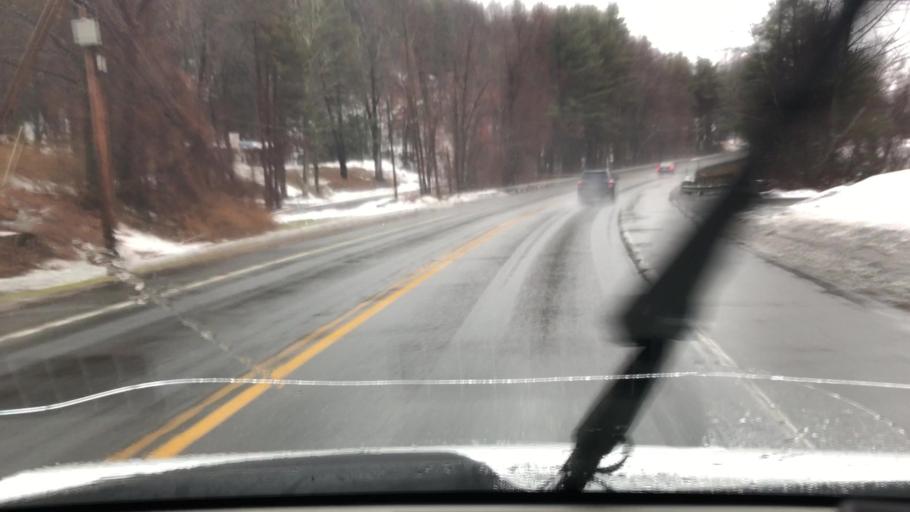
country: US
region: Massachusetts
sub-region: Franklin County
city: Shelburne Falls
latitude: 42.5908
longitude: -72.7195
